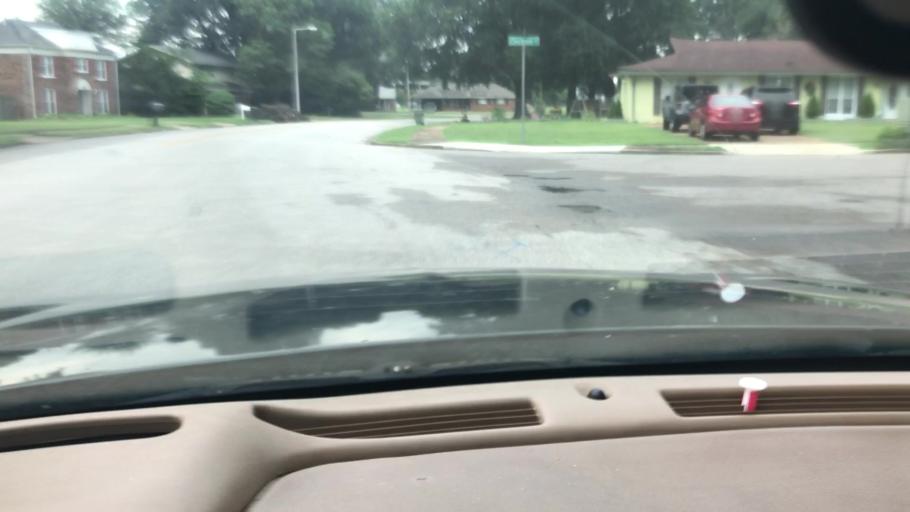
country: US
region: Tennessee
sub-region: Shelby County
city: Germantown
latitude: 35.0729
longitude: -89.8990
